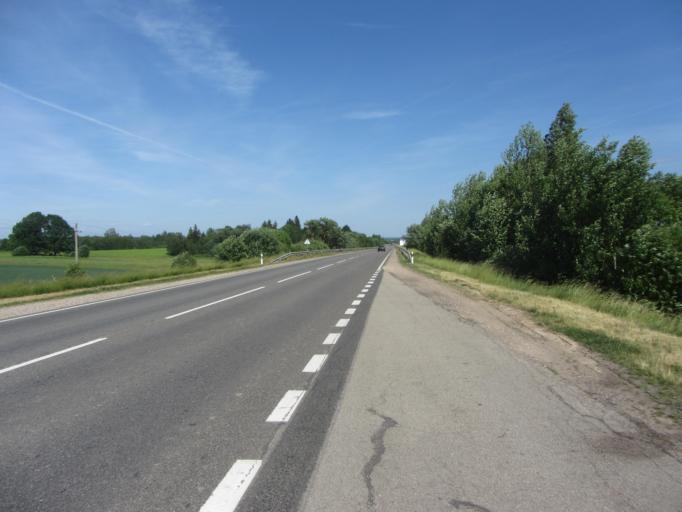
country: LT
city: Birstonas
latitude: 54.5801
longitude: 24.0795
